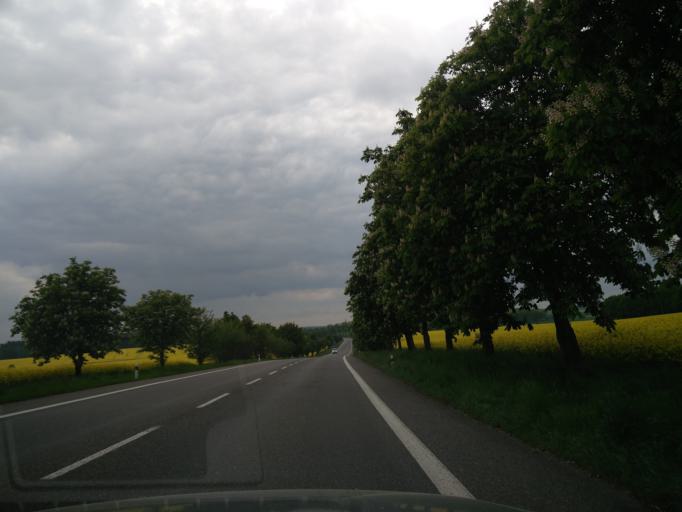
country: CZ
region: Jihocesky
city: Cimelice
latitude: 49.4572
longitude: 14.0657
